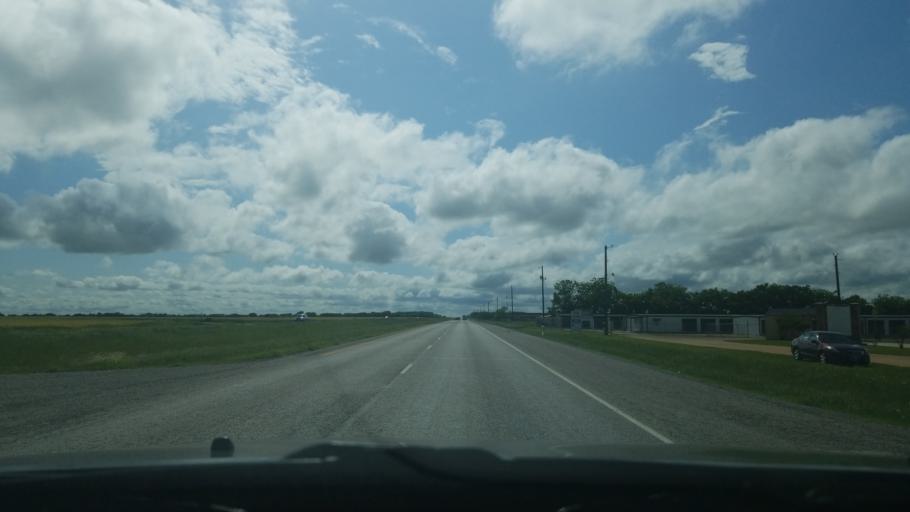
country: US
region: Texas
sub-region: Denton County
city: Ponder
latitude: 33.2378
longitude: -97.3038
